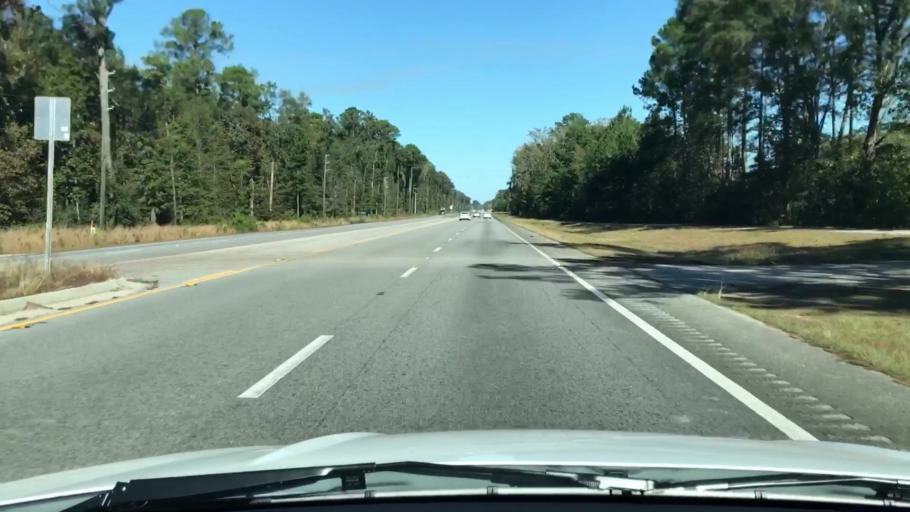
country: US
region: South Carolina
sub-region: Hampton County
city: Yemassee
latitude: 32.6101
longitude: -80.7489
